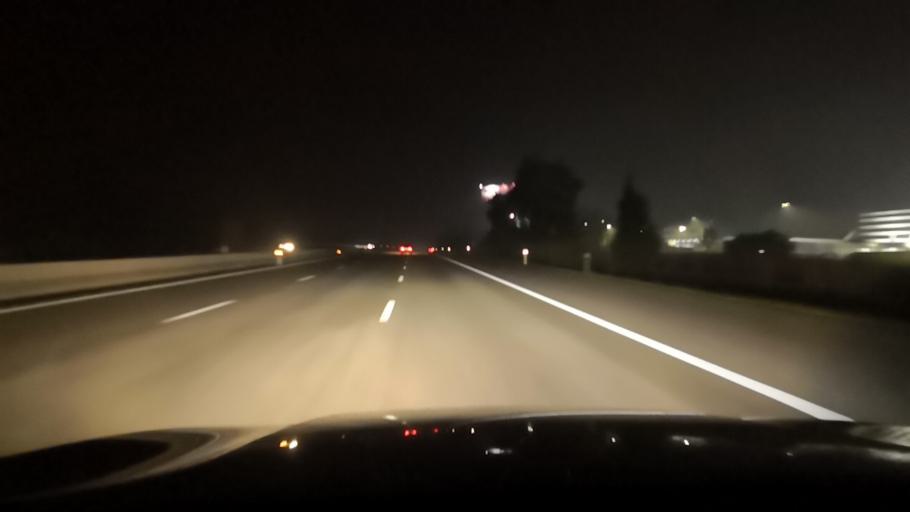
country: PT
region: Santarem
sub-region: Alcanena
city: Alcanena
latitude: 39.4442
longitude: -8.6298
